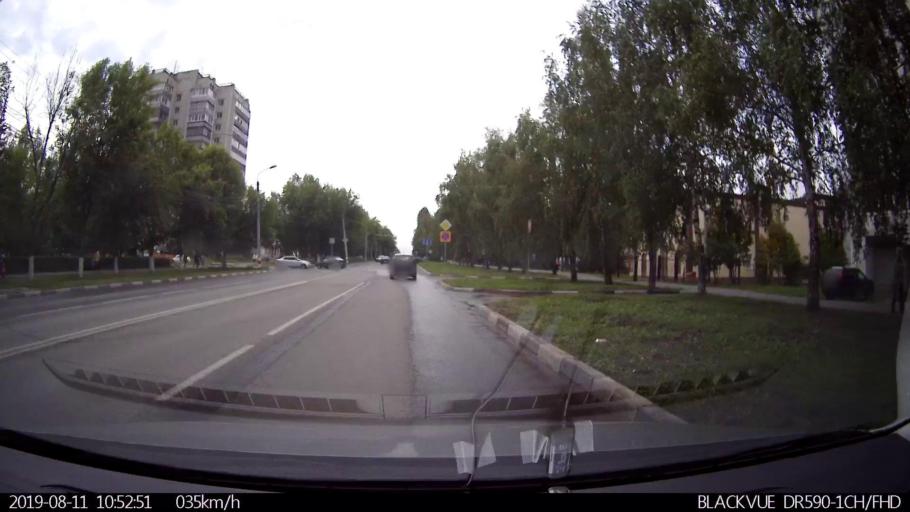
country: RU
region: Ulyanovsk
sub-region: Ulyanovskiy Rayon
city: Ulyanovsk
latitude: 54.2627
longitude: 48.3344
